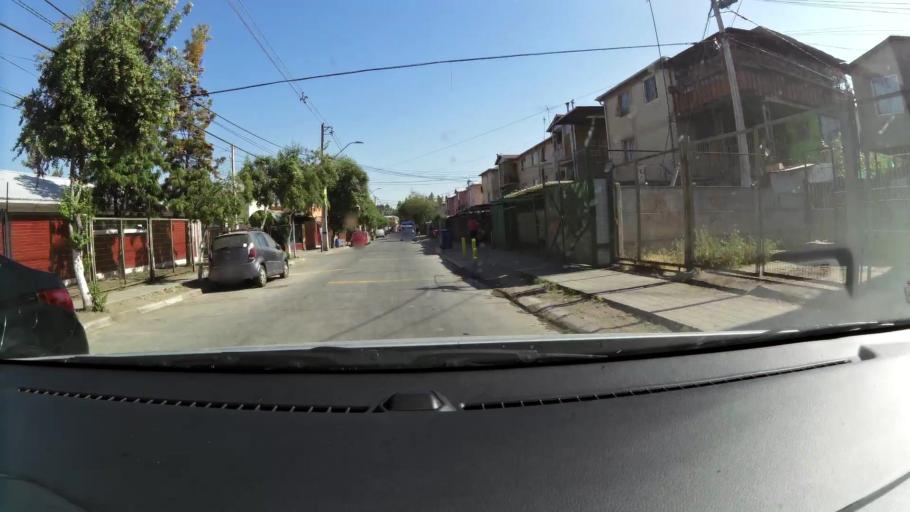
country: CL
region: Santiago Metropolitan
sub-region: Provincia de Maipo
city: San Bernardo
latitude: -33.5647
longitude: -70.7051
